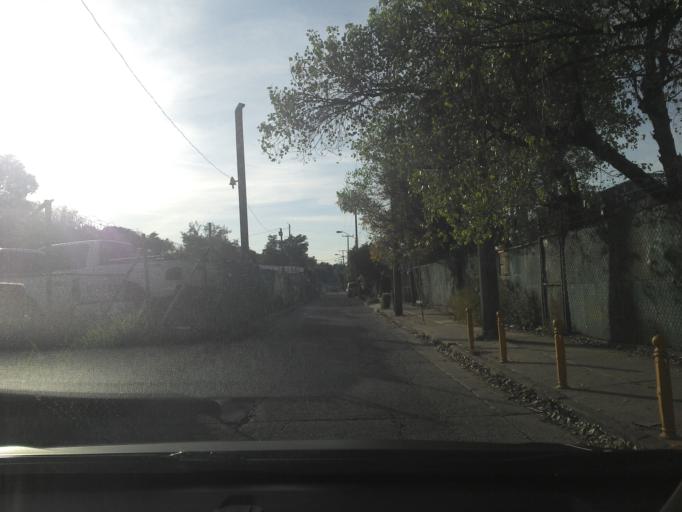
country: MX
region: Jalisco
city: Tlaquepaque
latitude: 20.6203
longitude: -103.3234
